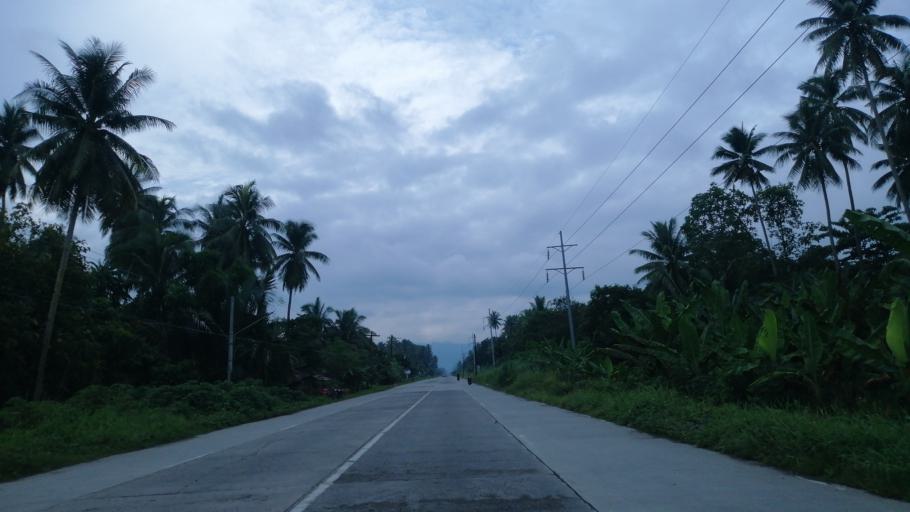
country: PH
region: Davao
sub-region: Province of Davao del Norte
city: Corocotan
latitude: 7.3948
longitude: 125.7829
